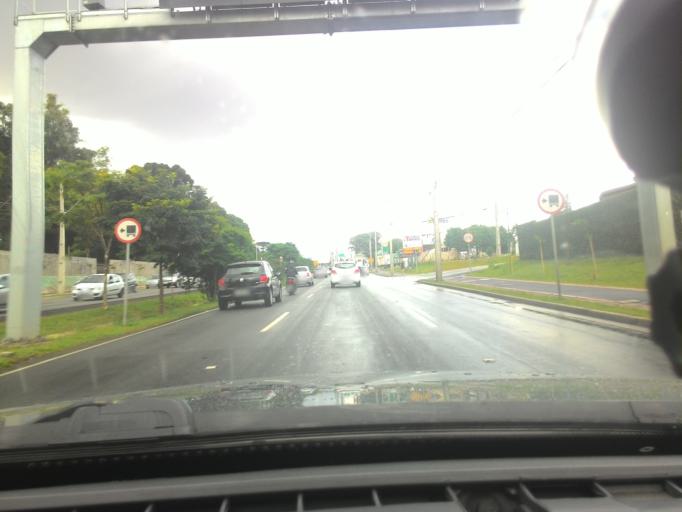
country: BR
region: Parana
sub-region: Sao Jose Dos Pinhais
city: Sao Jose dos Pinhais
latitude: -25.4943
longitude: -49.2130
